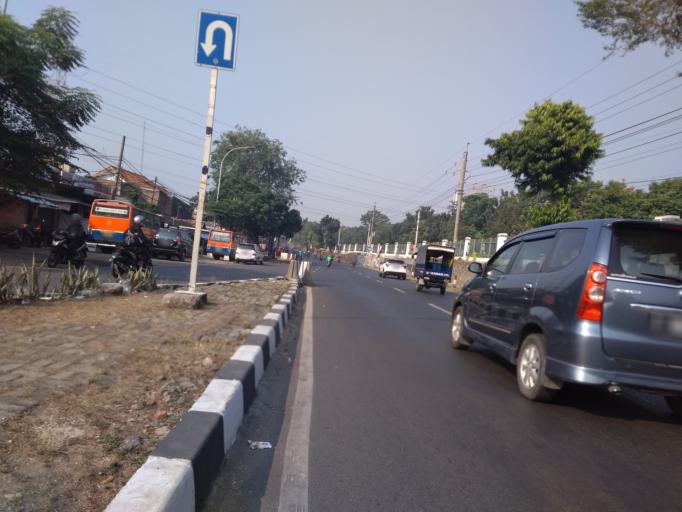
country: ID
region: Jakarta Raya
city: Jakarta
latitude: -6.2945
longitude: 106.8412
